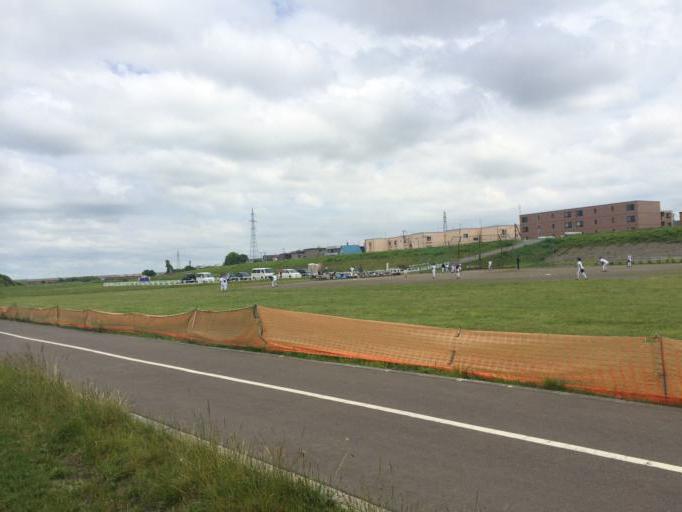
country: JP
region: Hokkaido
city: Sapporo
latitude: 43.0747
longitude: 141.4042
